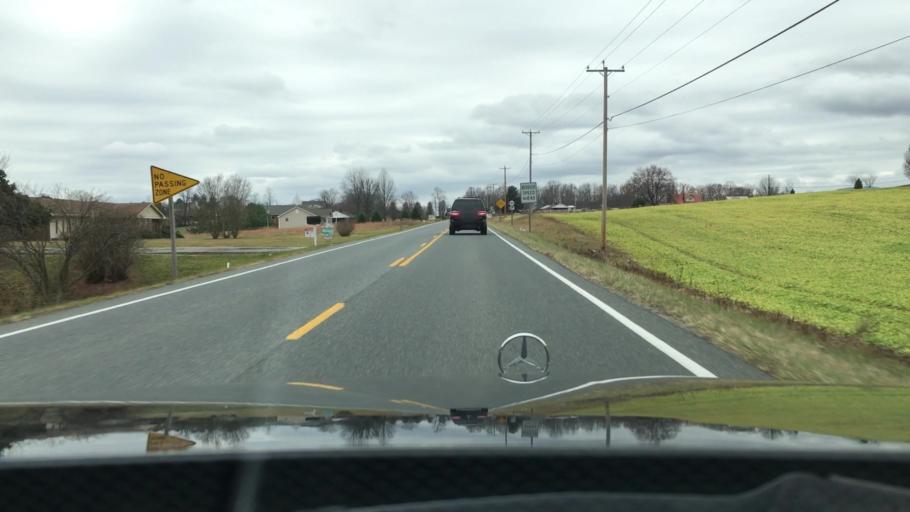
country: US
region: Virginia
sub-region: Botetourt County
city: Blue Ridge
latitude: 37.2503
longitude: -79.6951
